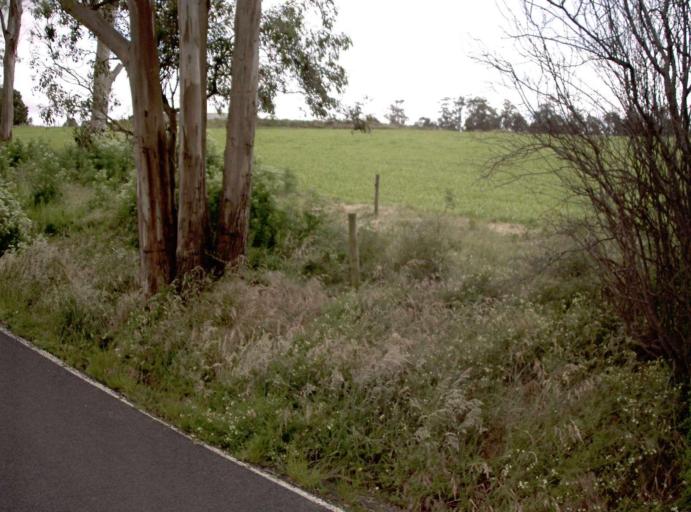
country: AU
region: Victoria
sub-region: Latrobe
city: Moe
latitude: -37.9613
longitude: 146.1332
